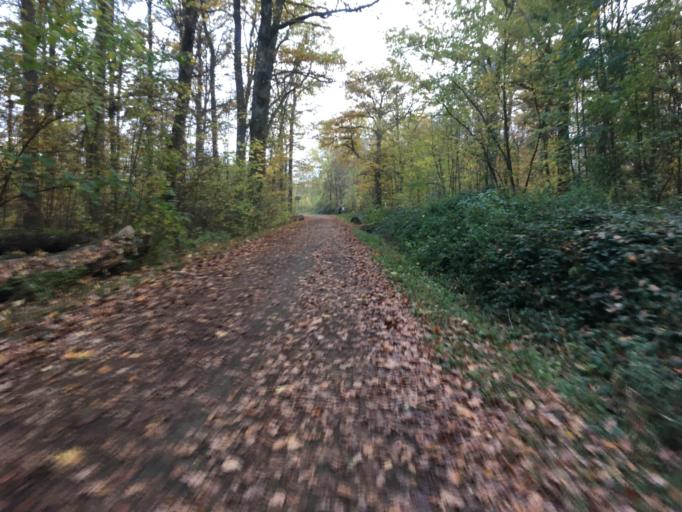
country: DE
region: Baden-Wuerttemberg
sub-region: Regierungsbezirk Stuttgart
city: Weinsberg
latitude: 49.1344
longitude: 9.2717
